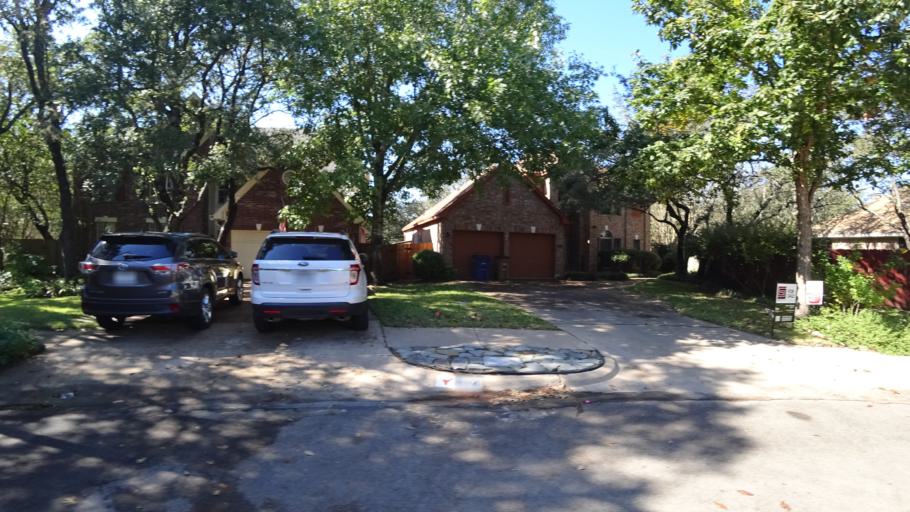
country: US
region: Texas
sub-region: Travis County
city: Shady Hollow
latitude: 30.2180
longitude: -97.8732
